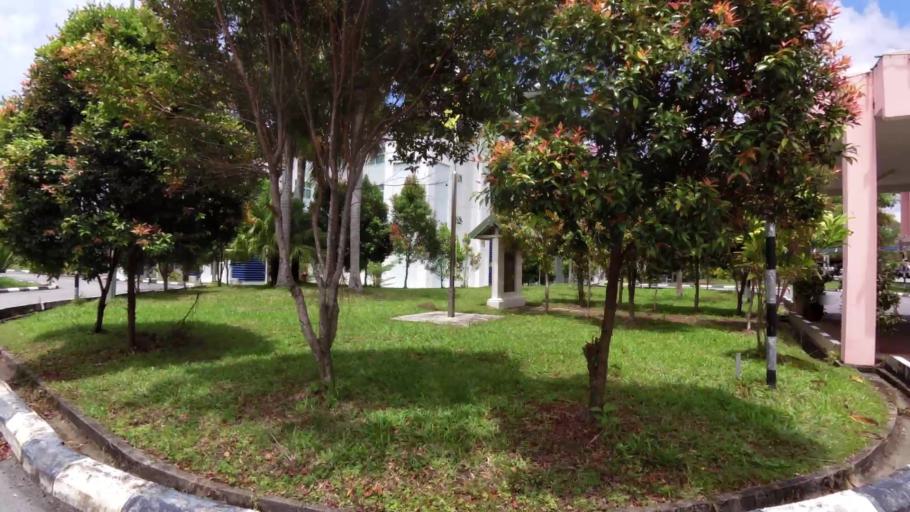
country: BN
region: Brunei and Muara
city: Bandar Seri Begawan
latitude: 4.9026
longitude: 114.9125
